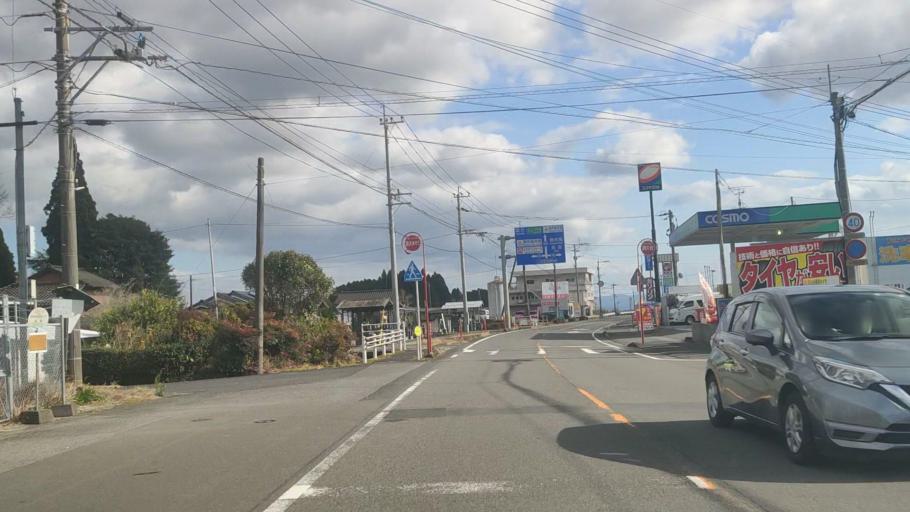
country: JP
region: Kagoshima
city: Kajiki
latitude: 31.8197
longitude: 130.7028
